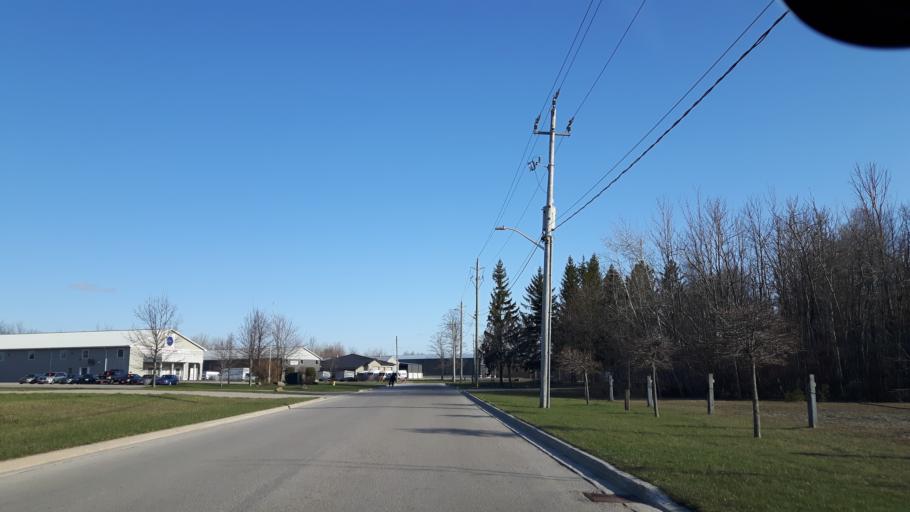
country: CA
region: Ontario
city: Goderich
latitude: 43.7299
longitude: -81.6946
